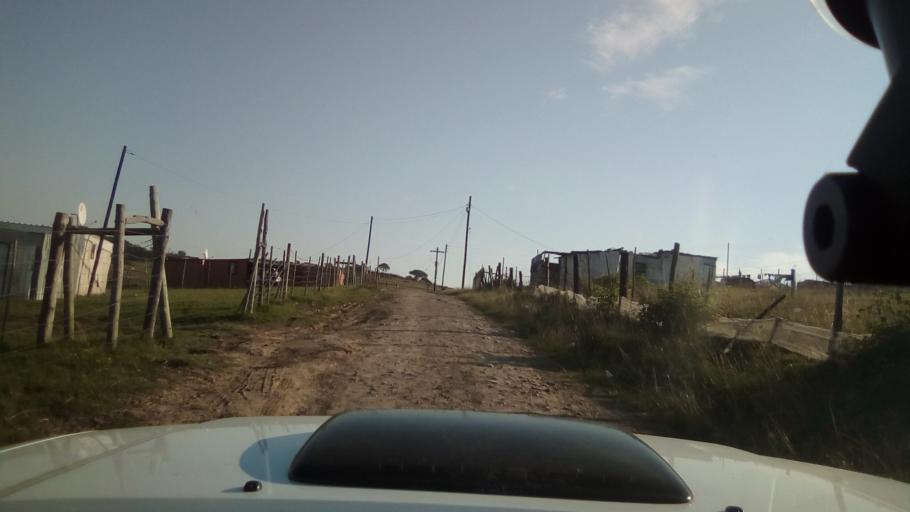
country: ZA
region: Eastern Cape
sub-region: Buffalo City Metropolitan Municipality
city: East London
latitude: -32.8464
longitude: 27.9858
